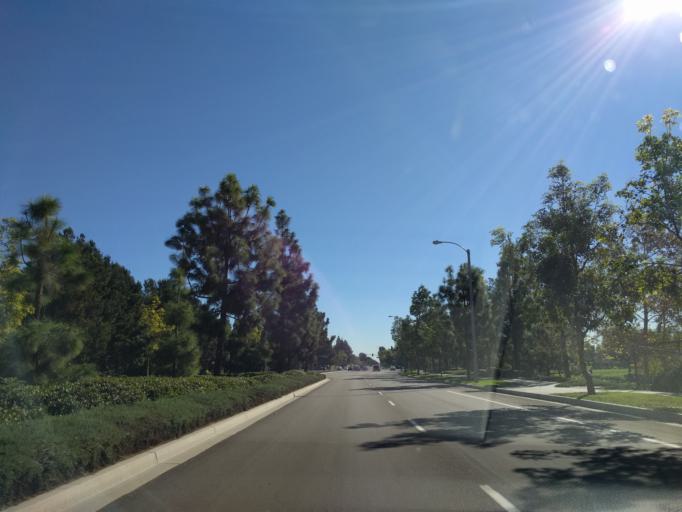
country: US
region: California
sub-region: Orange County
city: North Tustin
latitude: 33.7172
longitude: -117.7784
